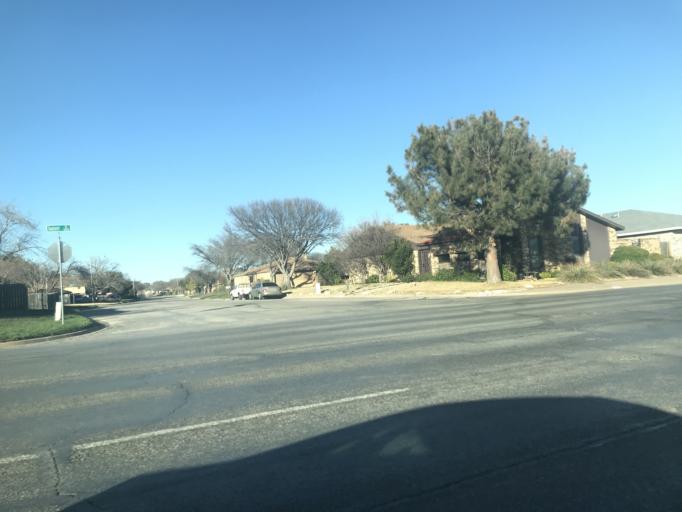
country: US
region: Texas
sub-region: Tom Green County
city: San Angelo
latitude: 31.4268
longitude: -100.4906
